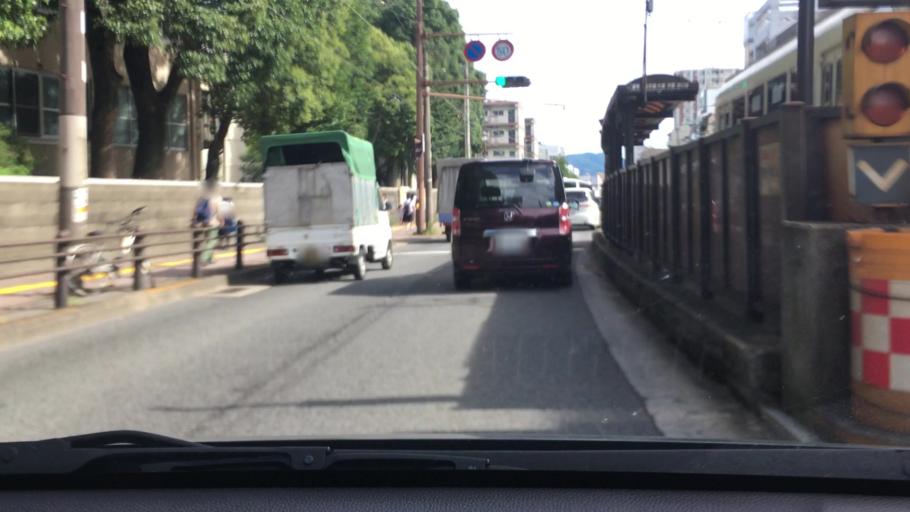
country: JP
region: Nagasaki
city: Obita
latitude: 32.7852
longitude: 129.8625
